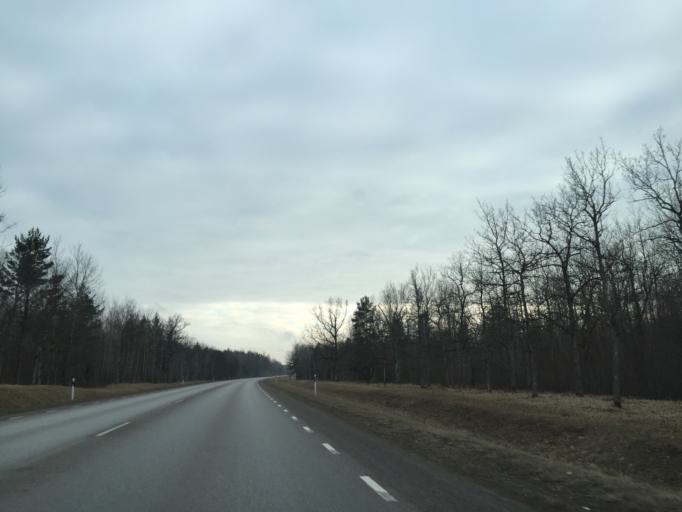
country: EE
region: Saare
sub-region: Orissaare vald
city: Orissaare
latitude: 58.4626
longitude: 22.8125
